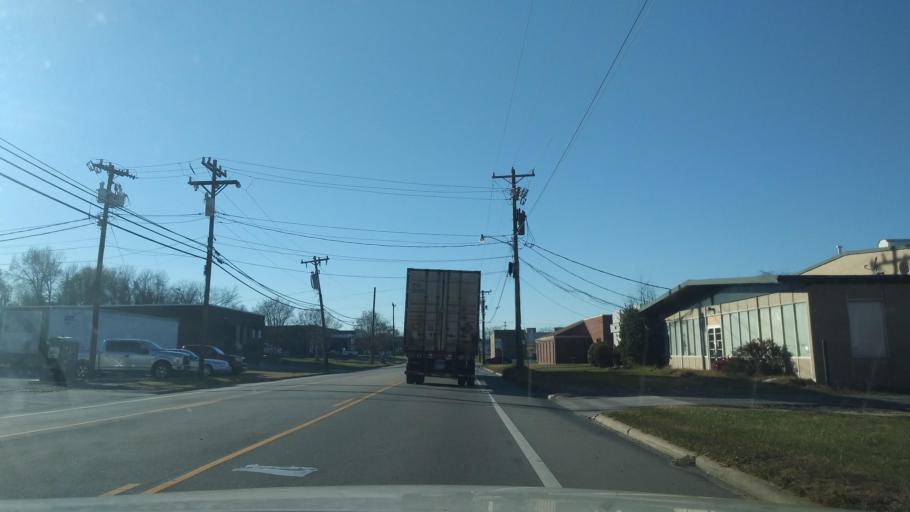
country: US
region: North Carolina
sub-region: Guilford County
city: Greensboro
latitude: 36.0291
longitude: -79.7880
